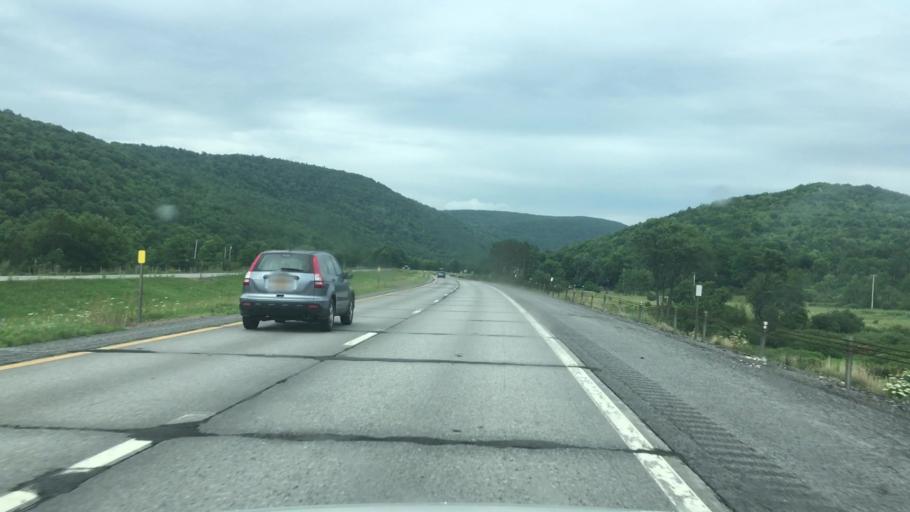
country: US
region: New York
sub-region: Otsego County
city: Worcester
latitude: 42.6253
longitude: -74.6618
